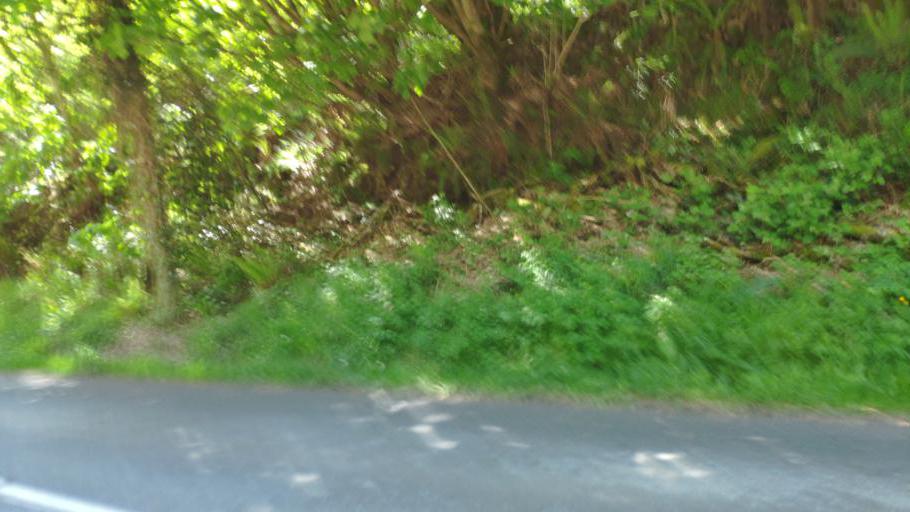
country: IE
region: Munster
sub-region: County Cork
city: Blarney
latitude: 51.9487
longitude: -8.5719
